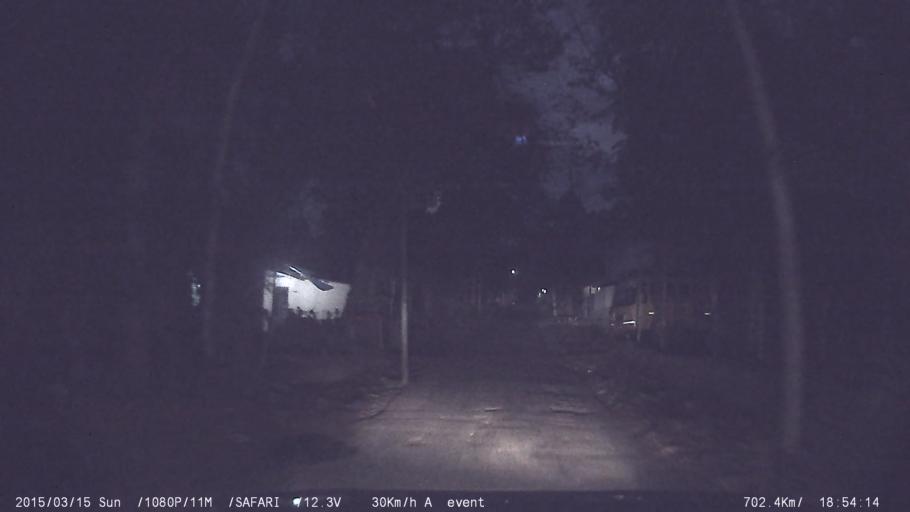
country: IN
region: Kerala
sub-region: Kottayam
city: Palackattumala
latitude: 9.8550
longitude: 76.6820
